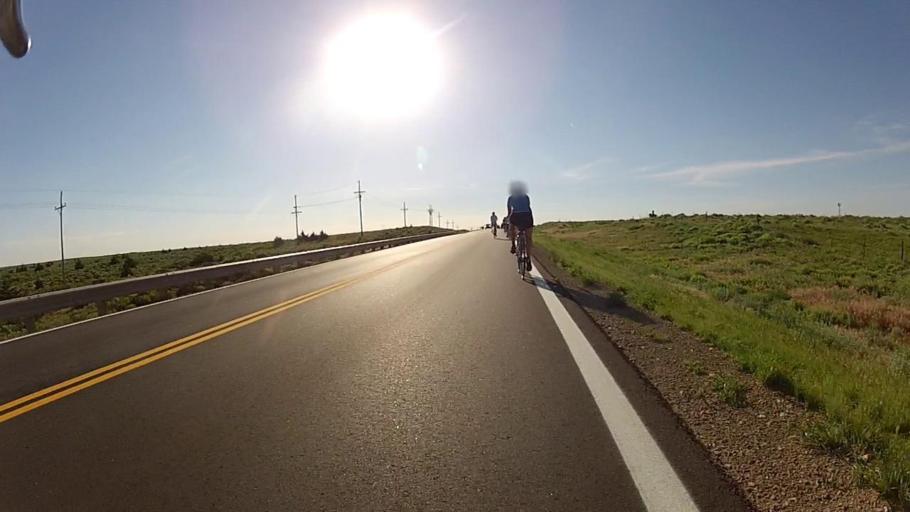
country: US
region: Kansas
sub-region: Comanche County
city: Coldwater
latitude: 37.2803
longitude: -99.0155
